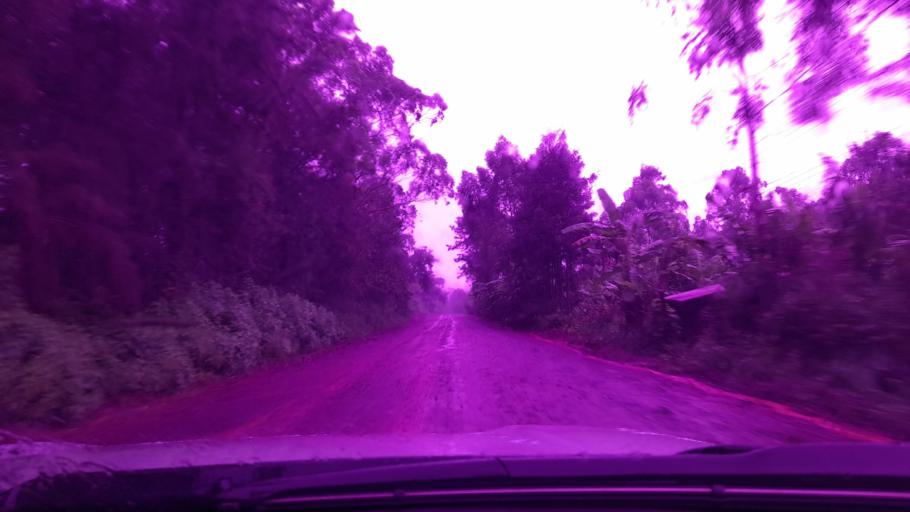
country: ET
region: Oromiya
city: Metu
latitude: 8.3213
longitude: 35.6003
